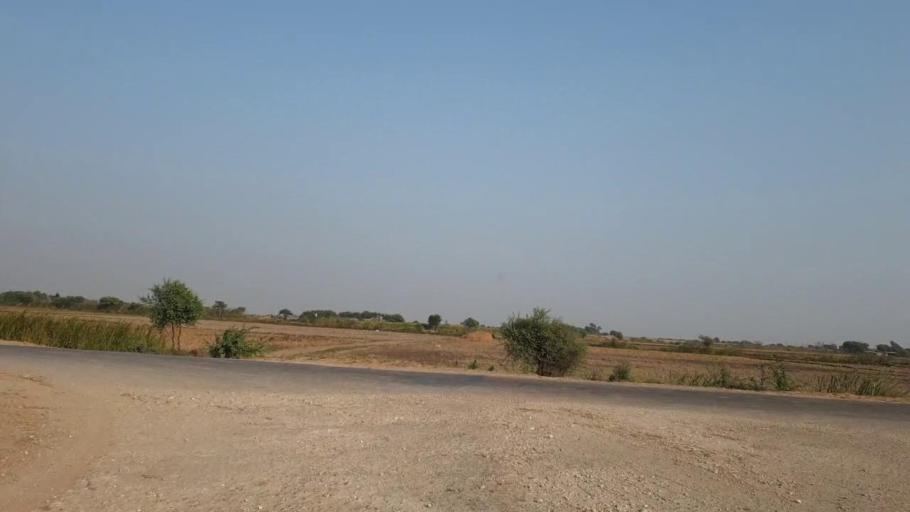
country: PK
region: Sindh
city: Tando Muhammad Khan
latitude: 24.9500
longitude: 68.4942
